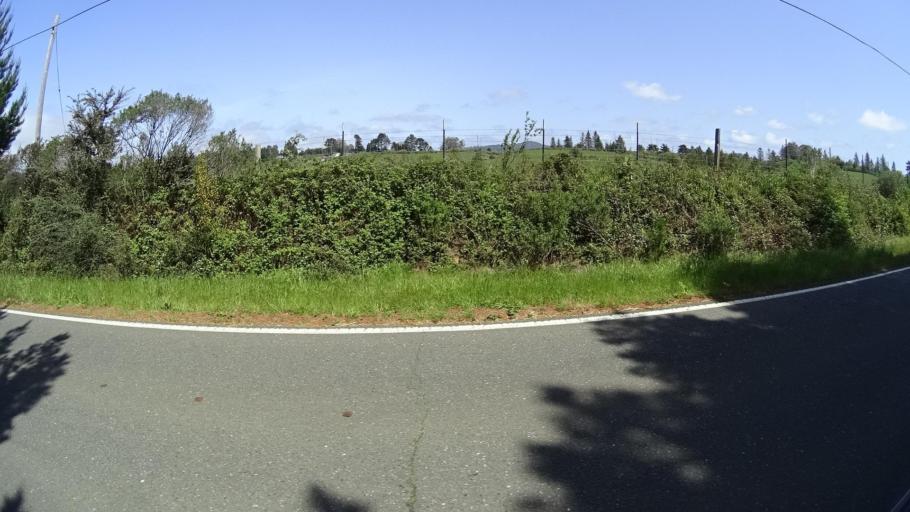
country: US
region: California
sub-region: Humboldt County
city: Fortuna
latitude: 40.6439
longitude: -124.2147
